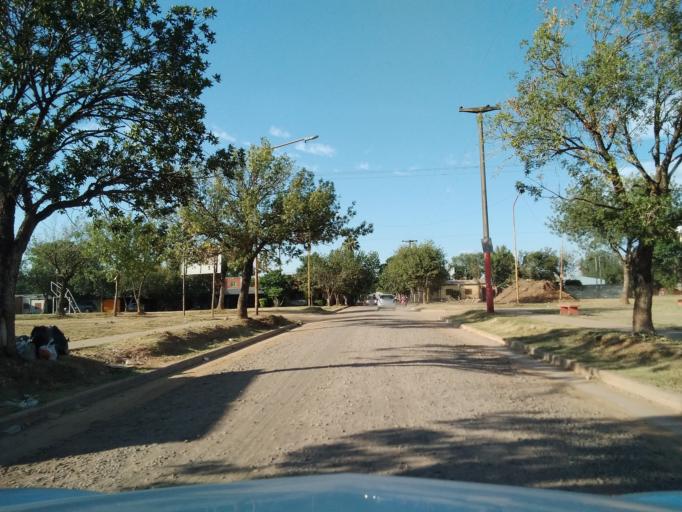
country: AR
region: Corrientes
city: Corrientes
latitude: -27.4916
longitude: -58.7833
